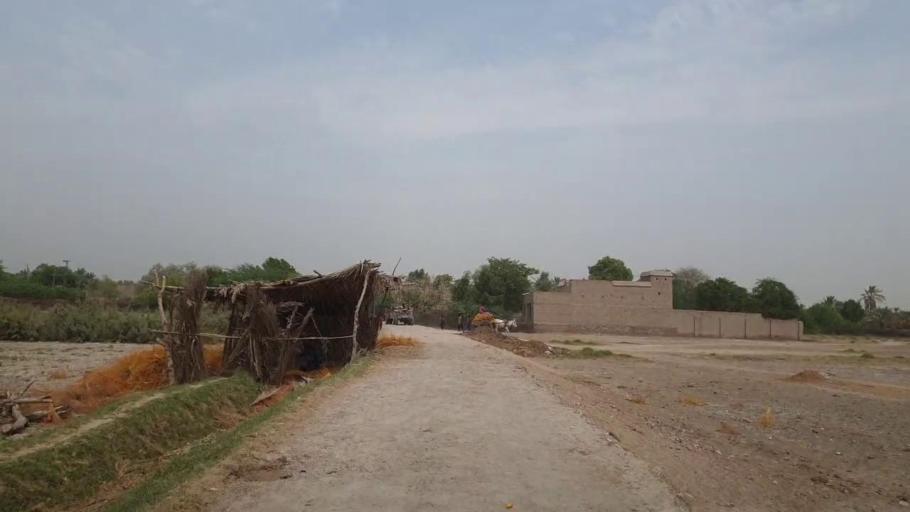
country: PK
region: Sindh
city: Pir jo Goth
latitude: 27.5184
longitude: 68.5849
